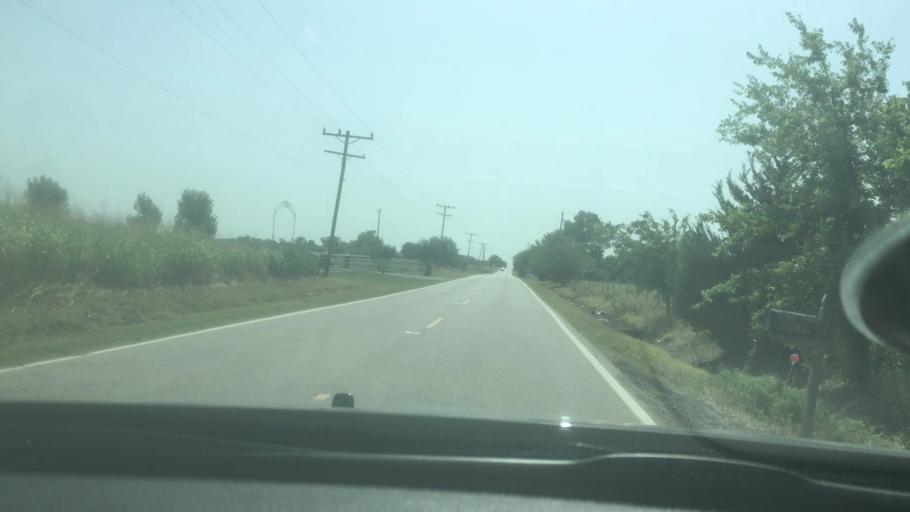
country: US
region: Oklahoma
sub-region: Bryan County
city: Durant
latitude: 34.0848
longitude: -96.4297
